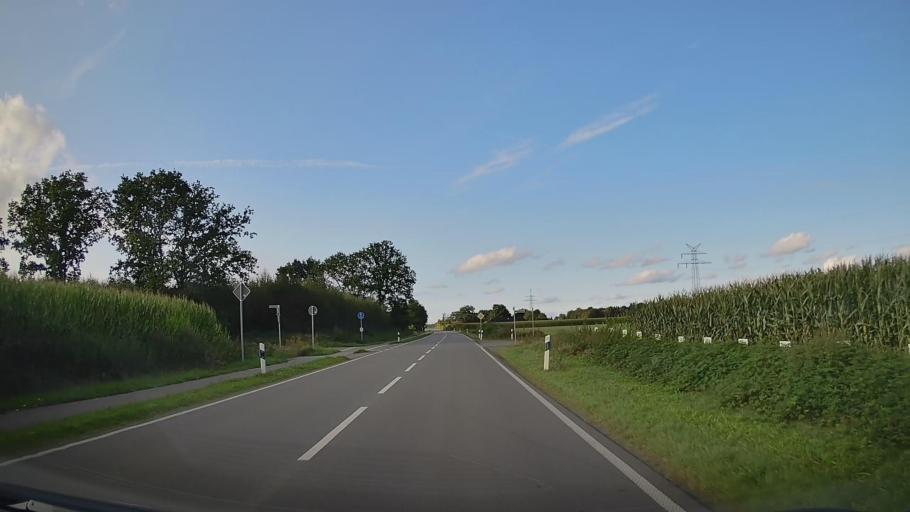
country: DE
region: Lower Saxony
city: Barssel
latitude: 53.1046
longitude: 7.7091
